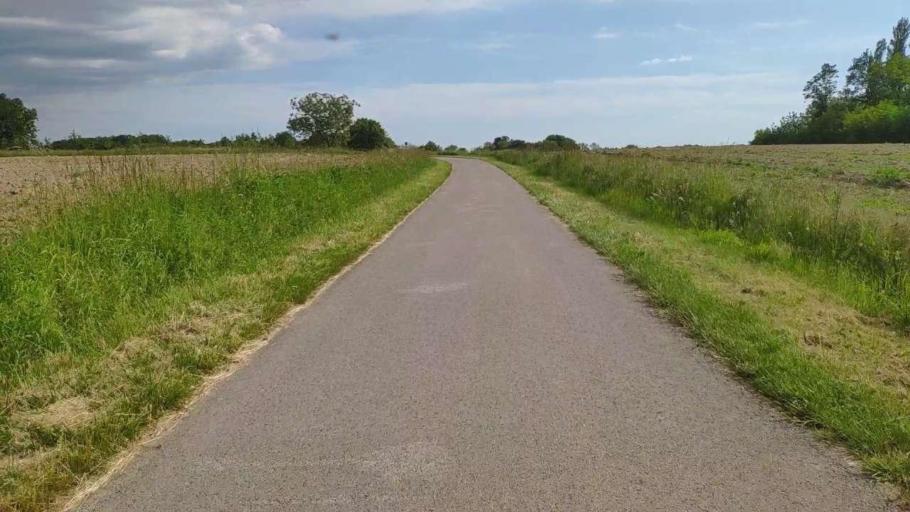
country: FR
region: Bourgogne
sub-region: Departement de Saone-et-Loire
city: Pierre-de-Bresse
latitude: 46.8200
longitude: 5.3399
